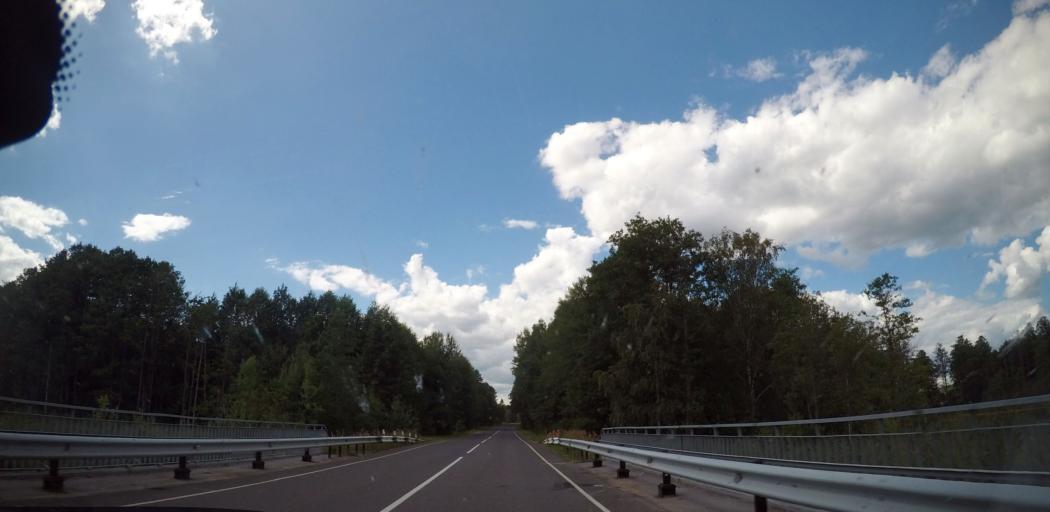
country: LT
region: Alytaus apskritis
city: Druskininkai
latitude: 53.8713
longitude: 24.1590
